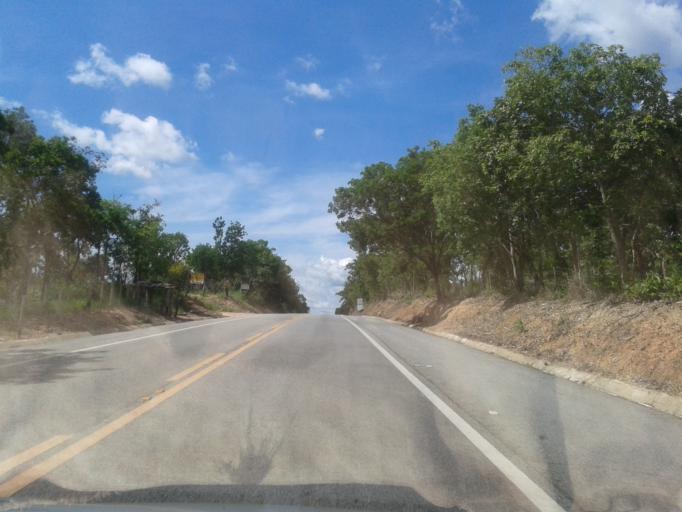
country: BR
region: Goias
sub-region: Goias
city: Goias
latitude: -15.7279
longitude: -50.1859
